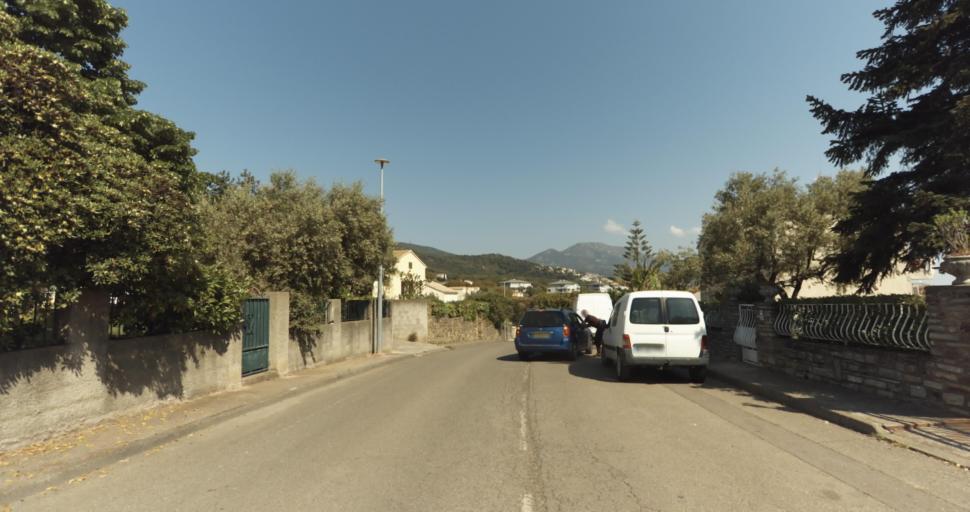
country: FR
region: Corsica
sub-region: Departement de la Haute-Corse
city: Biguglia
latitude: 42.6261
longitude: 9.4290
